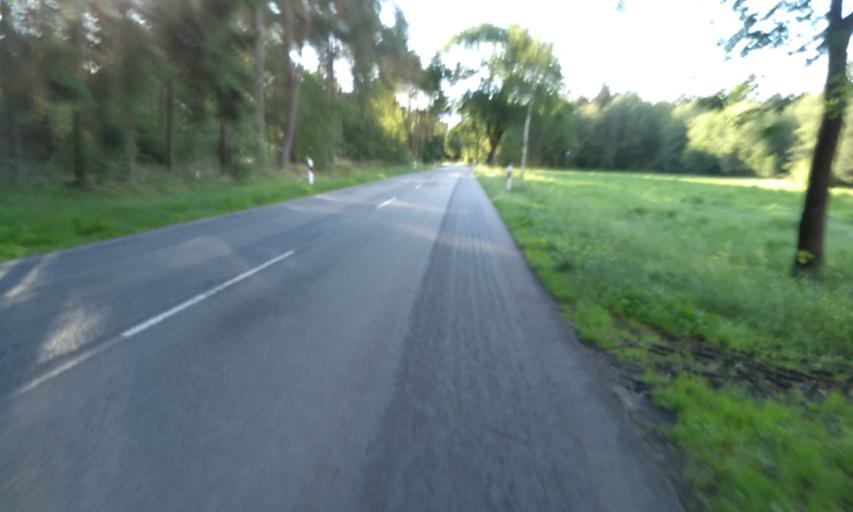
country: DE
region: Lower Saxony
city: Heeslingen
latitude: 53.3573
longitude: 9.3407
